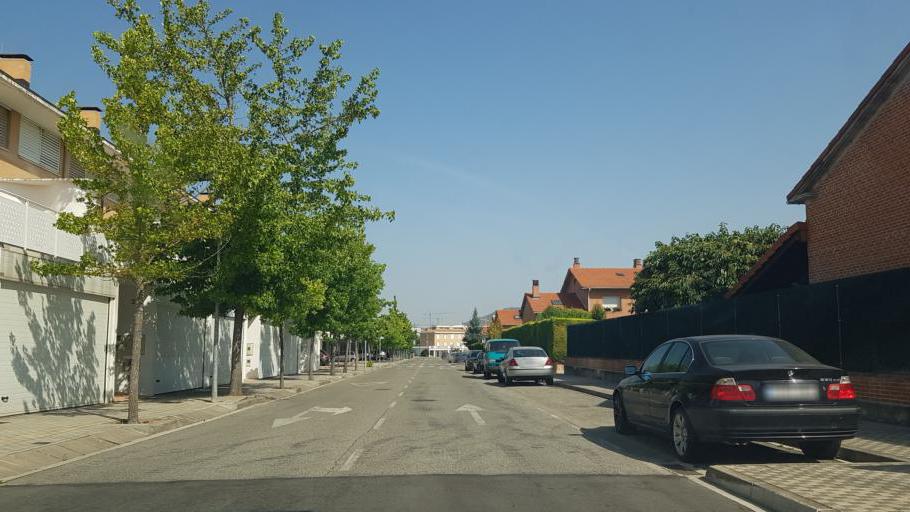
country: ES
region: Navarre
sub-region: Provincia de Navarra
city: Segundo Ensanche
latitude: 42.7929
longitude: -1.6237
